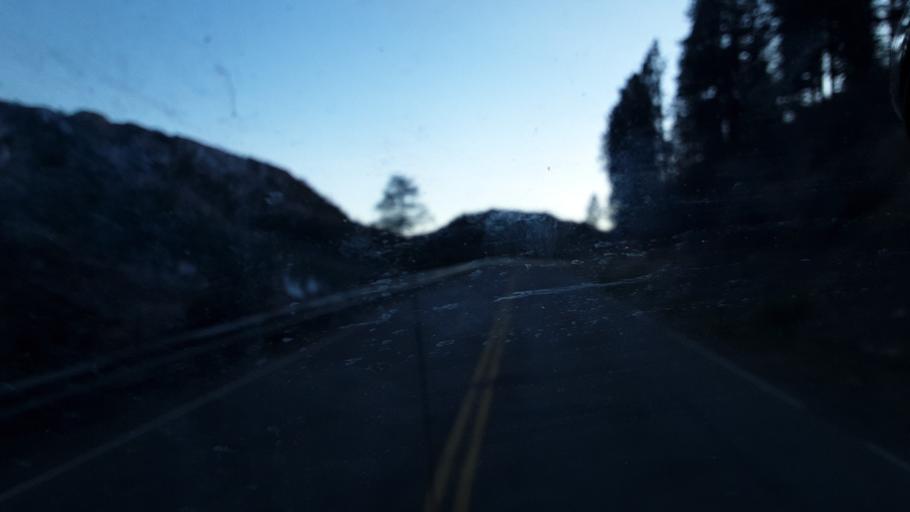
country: US
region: Colorado
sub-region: La Plata County
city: Durango
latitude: 37.3165
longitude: -107.7709
